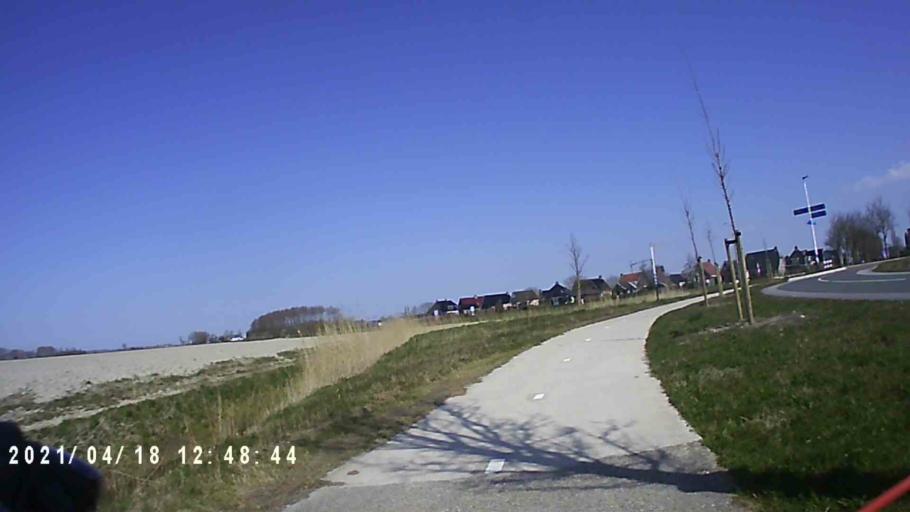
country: NL
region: Friesland
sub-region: Gemeente Dongeradeel
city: Dokkum
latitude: 53.3743
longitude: 6.0515
